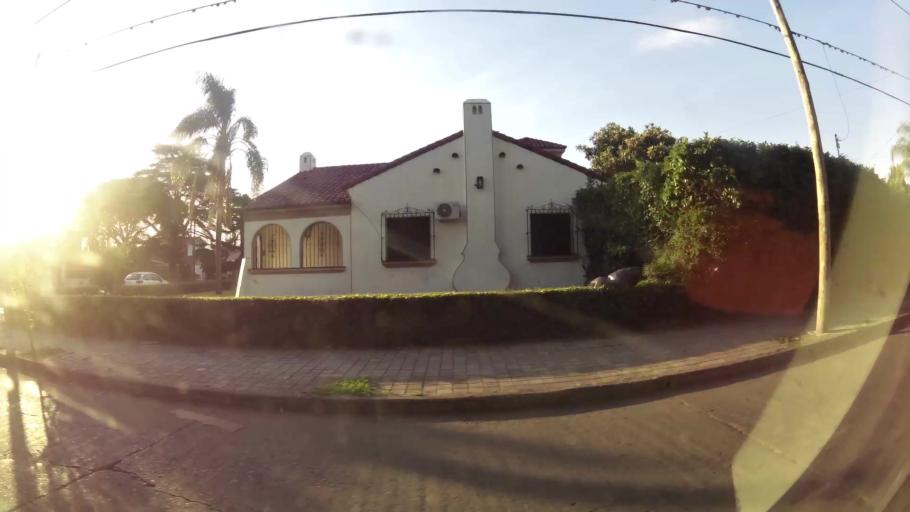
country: AR
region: Cordoba
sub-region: Departamento de Capital
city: Cordoba
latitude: -31.3761
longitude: -64.2316
